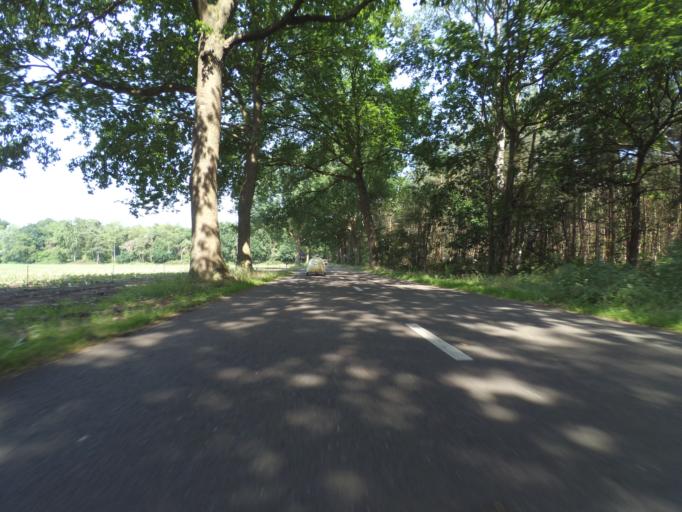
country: NL
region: North Brabant
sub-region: Gemeente Breda
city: Breda
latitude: 51.5286
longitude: 4.7617
